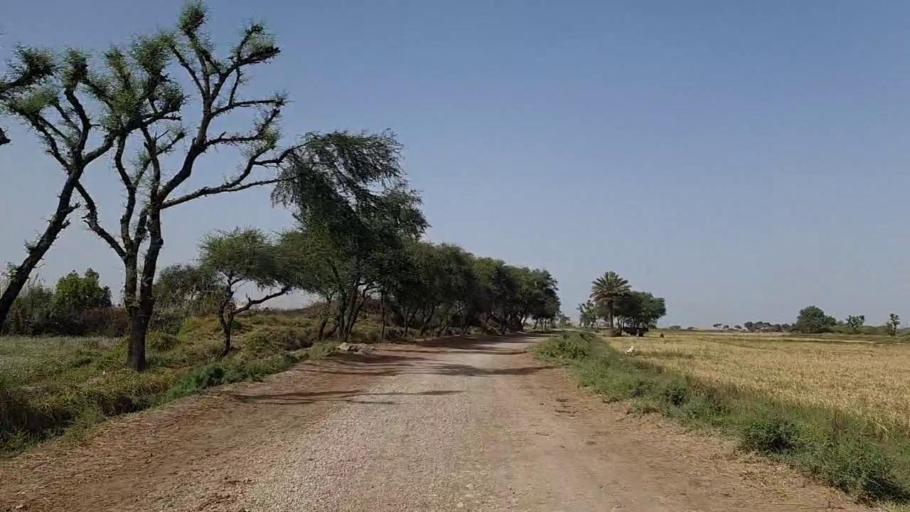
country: PK
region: Sindh
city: Jati
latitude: 24.3420
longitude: 68.3040
